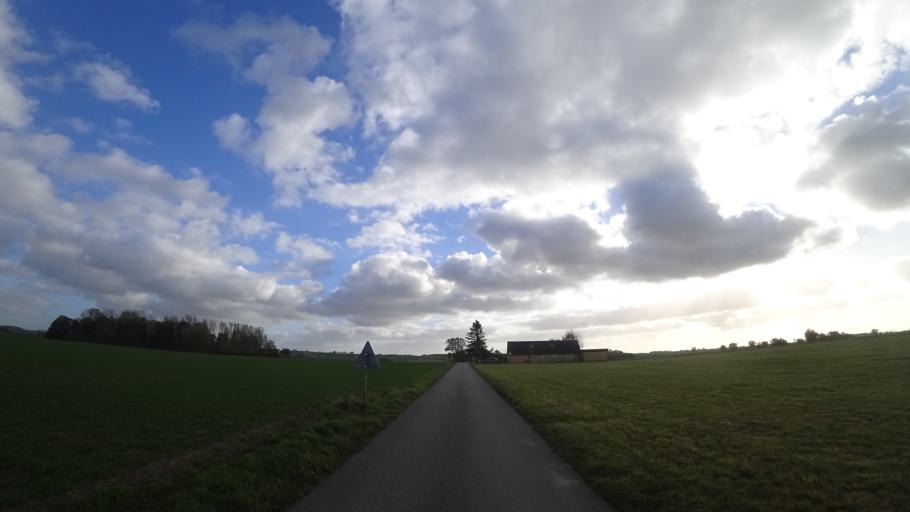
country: SE
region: Skane
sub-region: Staffanstorps Kommun
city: Staffanstorp
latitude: 55.6201
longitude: 13.2046
